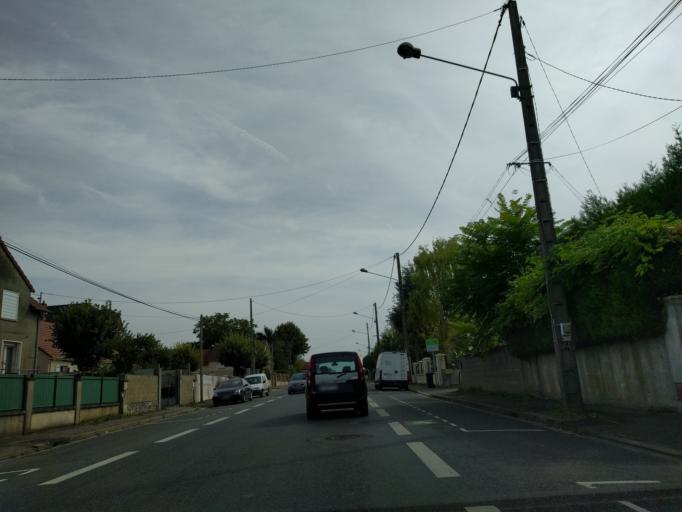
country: FR
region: Centre
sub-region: Departement du Cher
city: Bourges
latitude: 47.0630
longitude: 2.4217
